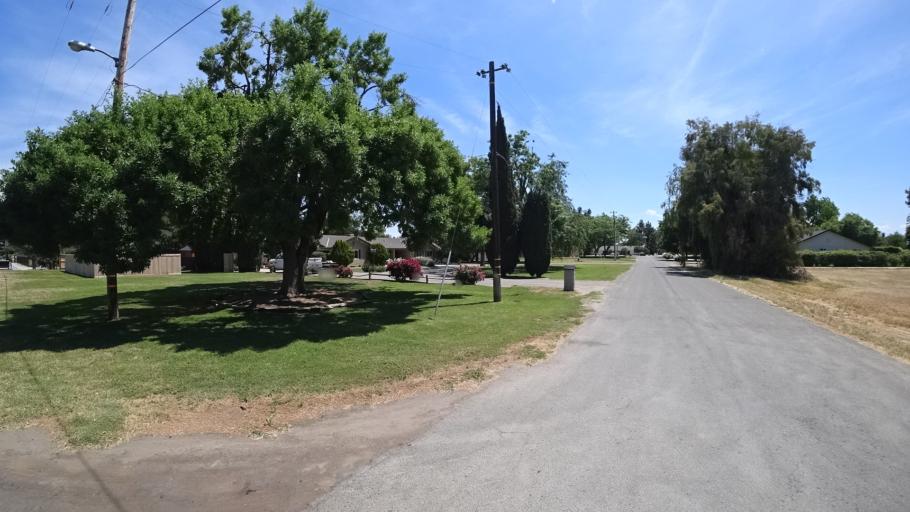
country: US
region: California
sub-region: Kings County
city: Lemoore
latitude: 36.2872
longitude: -119.7792
